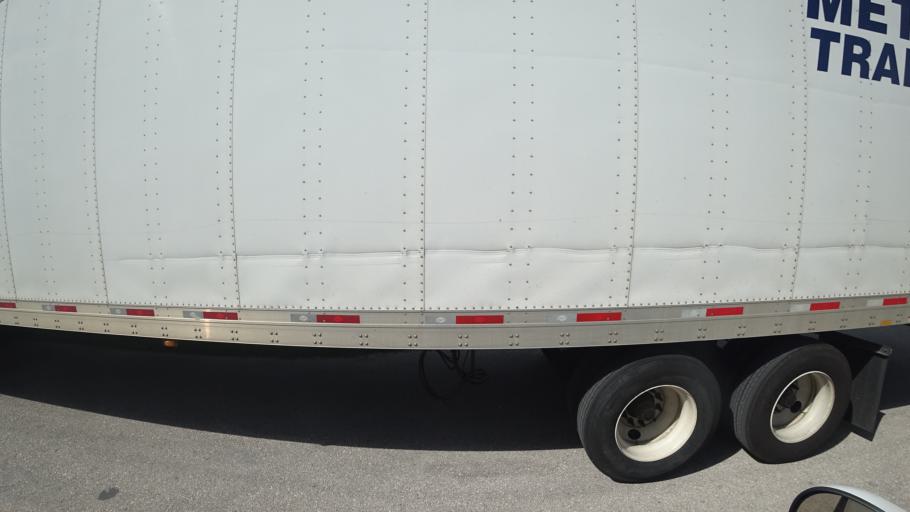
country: US
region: Florida
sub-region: Manatee County
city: West Samoset
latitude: 27.4744
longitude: -82.5502
